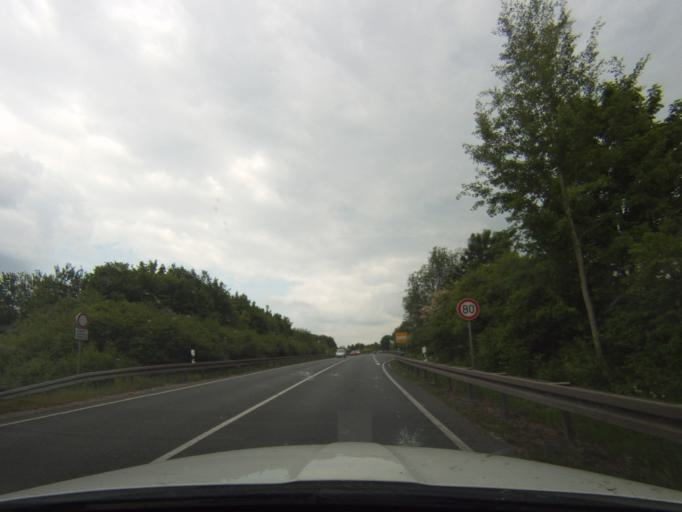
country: DE
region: Thuringia
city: Saalfeld
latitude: 50.6650
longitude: 11.3471
